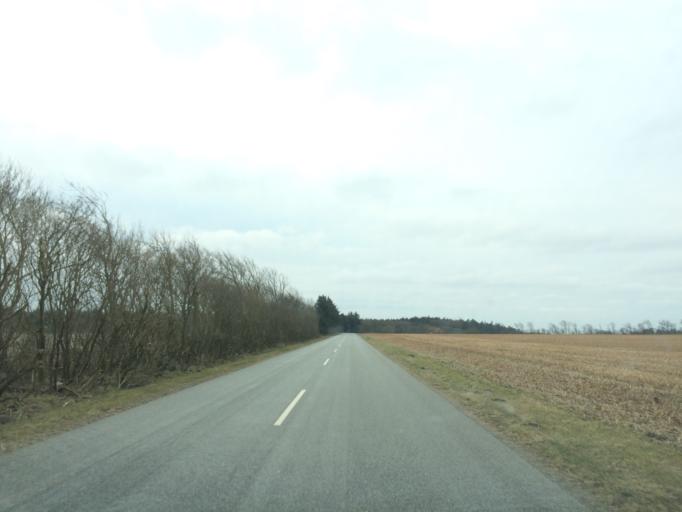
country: DK
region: Central Jutland
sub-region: Ringkobing-Skjern Kommune
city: Tarm
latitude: 55.8060
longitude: 8.3869
